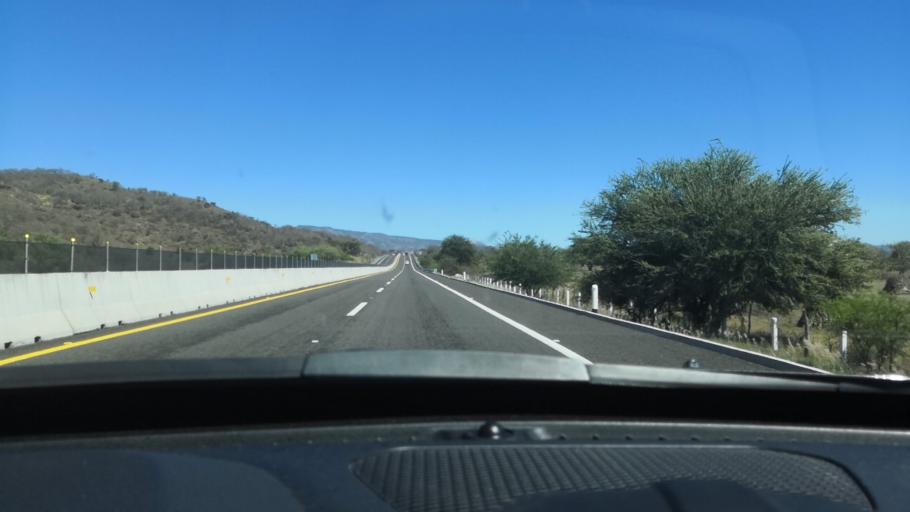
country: MX
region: Nayarit
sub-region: Ahuacatlan
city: Ahuacatlan
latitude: 21.0659
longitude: -104.4875
